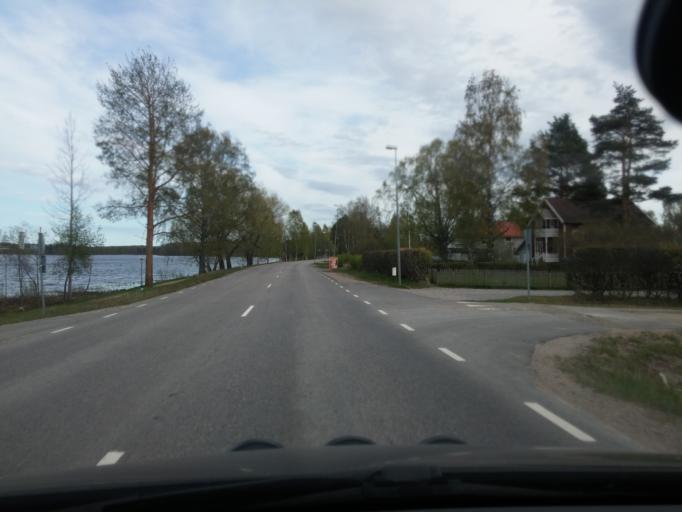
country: SE
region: Gaevleborg
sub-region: Ljusdals Kommun
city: Ljusdal
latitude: 61.8247
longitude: 16.0722
